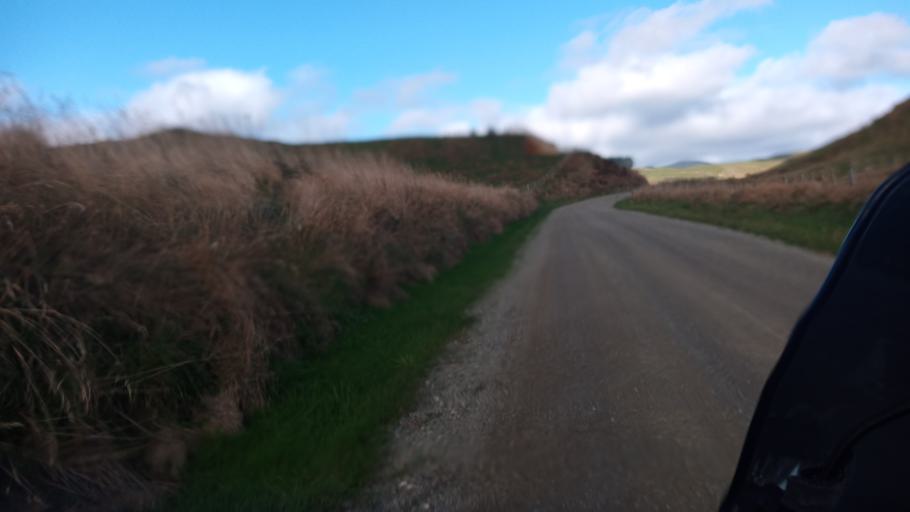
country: NZ
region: Bay of Plenty
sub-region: Opotiki District
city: Opotiki
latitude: -38.4546
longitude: 177.3942
